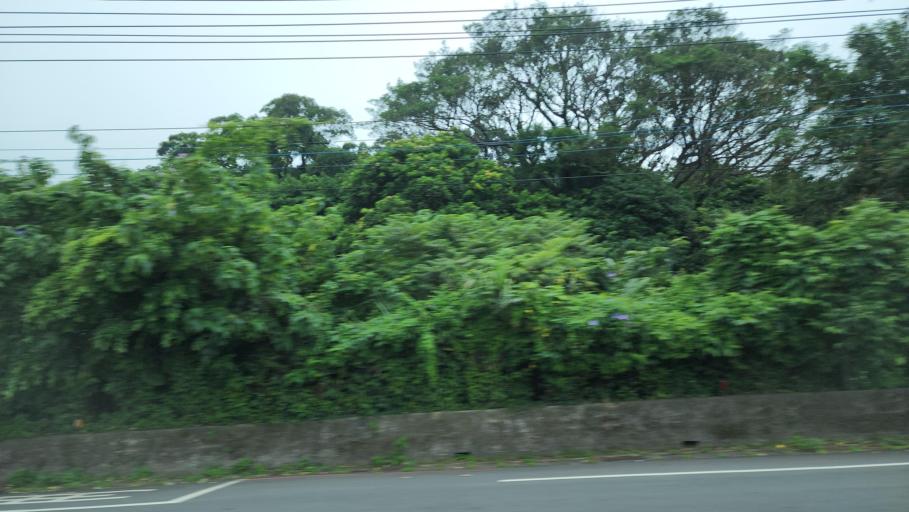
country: TW
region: Taiwan
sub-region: Keelung
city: Keelung
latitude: 25.1919
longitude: 121.6800
